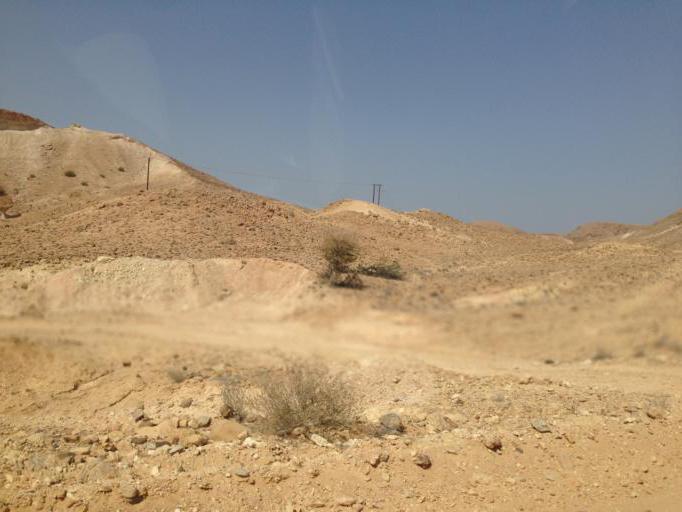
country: OM
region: Ash Sharqiyah
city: Ibra'
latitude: 23.0808
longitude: 58.9253
